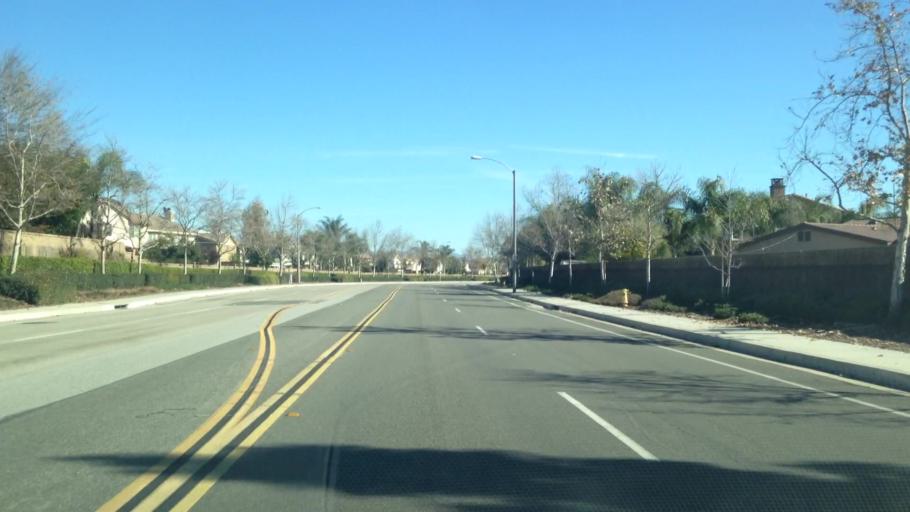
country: US
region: California
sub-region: Riverside County
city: Norco
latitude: 33.9681
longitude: -117.5729
